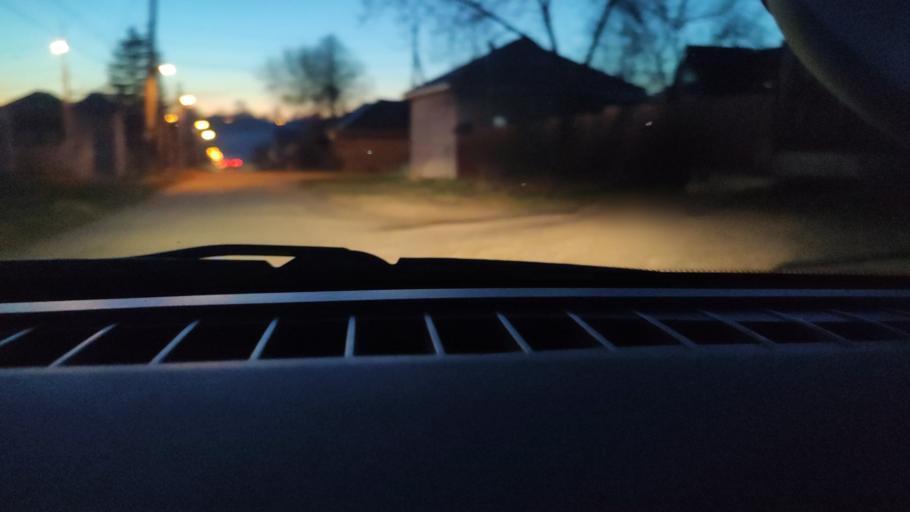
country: RU
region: Perm
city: Perm
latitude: 58.0402
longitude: 56.3361
